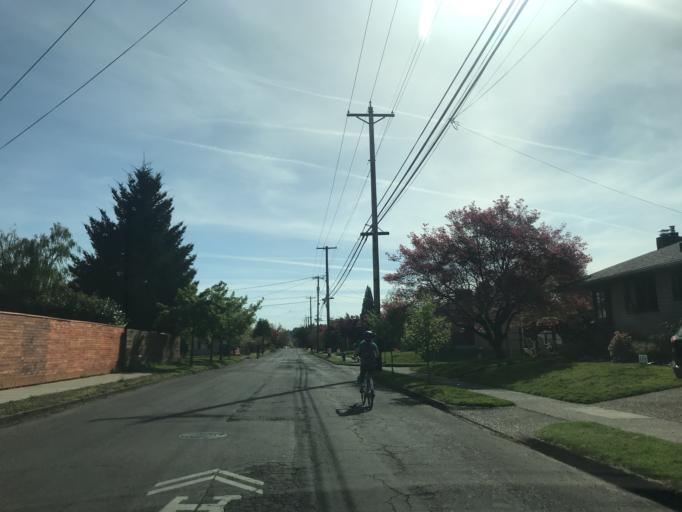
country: US
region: Oregon
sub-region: Multnomah County
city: Lents
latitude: 45.5014
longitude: -122.5985
